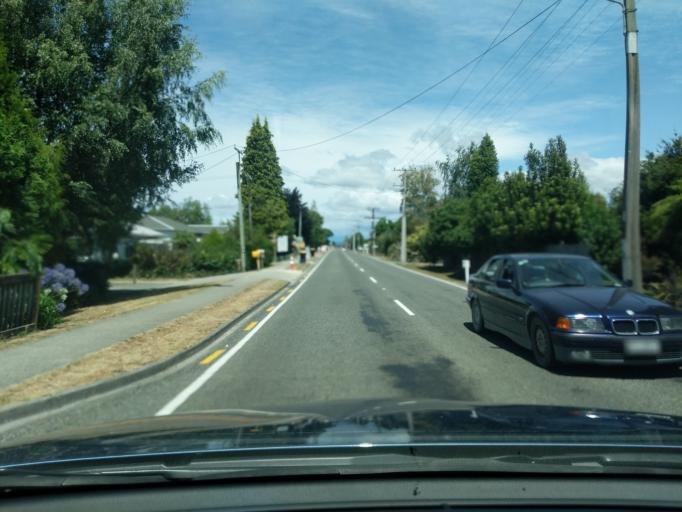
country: NZ
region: Tasman
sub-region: Tasman District
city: Motueka
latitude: -41.0834
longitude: 172.9971
